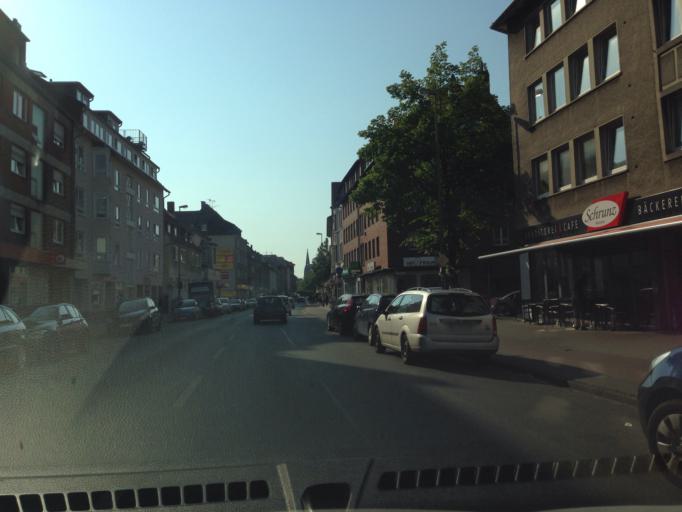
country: DE
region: North Rhine-Westphalia
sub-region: Regierungsbezirk Munster
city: Muenster
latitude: 51.9568
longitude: 7.6420
